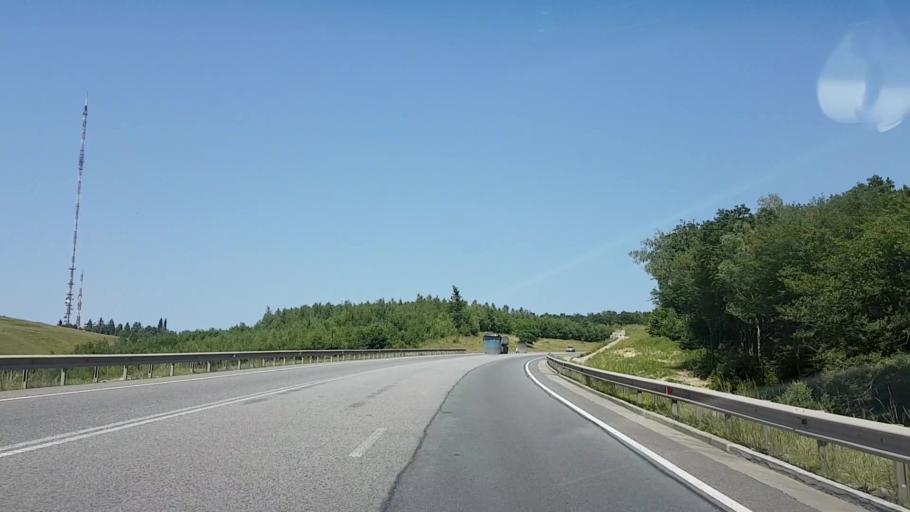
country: RO
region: Cluj
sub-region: Comuna Feleacu
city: Feleacu
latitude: 46.7066
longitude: 23.6430
